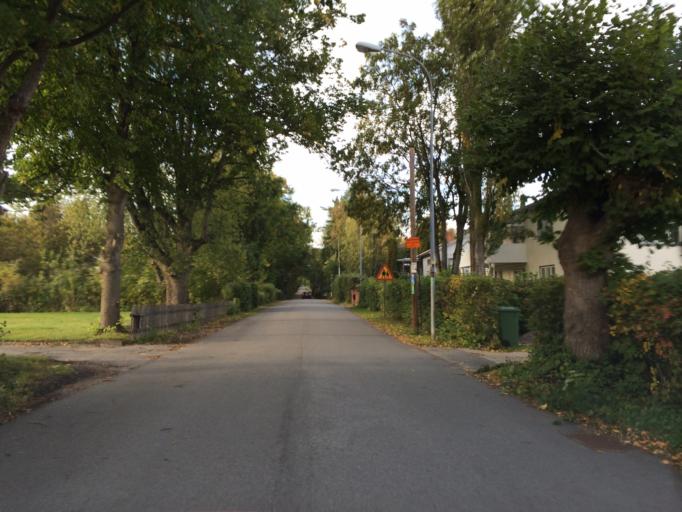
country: SE
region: Stockholm
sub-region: Sollentuna Kommun
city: Sollentuna
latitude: 59.4514
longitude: 17.9239
